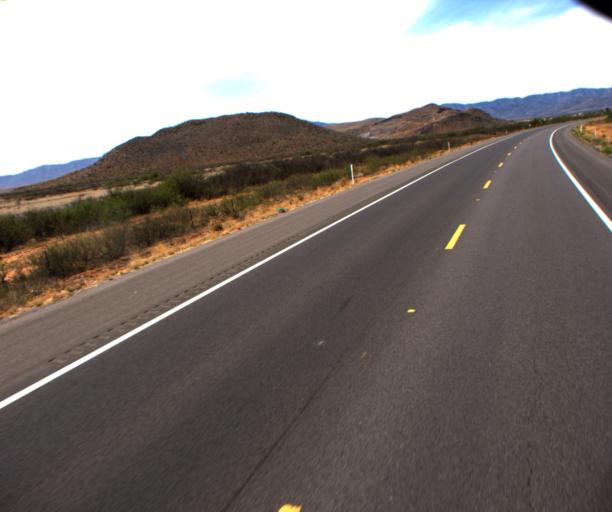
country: US
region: Arizona
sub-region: Cochise County
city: Tombstone
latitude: 31.9037
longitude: -109.7946
